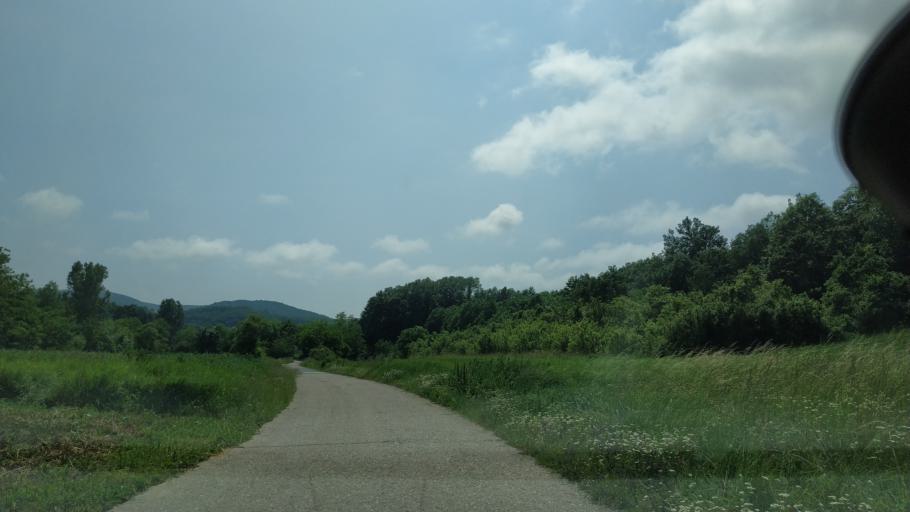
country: RS
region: Central Serbia
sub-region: Nisavski Okrug
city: Aleksinac
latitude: 43.4238
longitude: 21.7196
